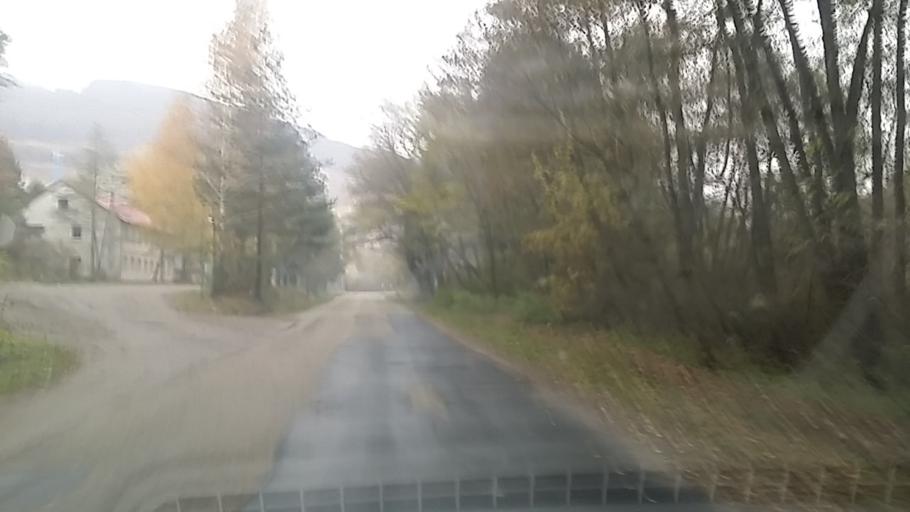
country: HU
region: Borsod-Abauj-Zemplen
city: Sarospatak
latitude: 48.4637
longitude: 21.4953
